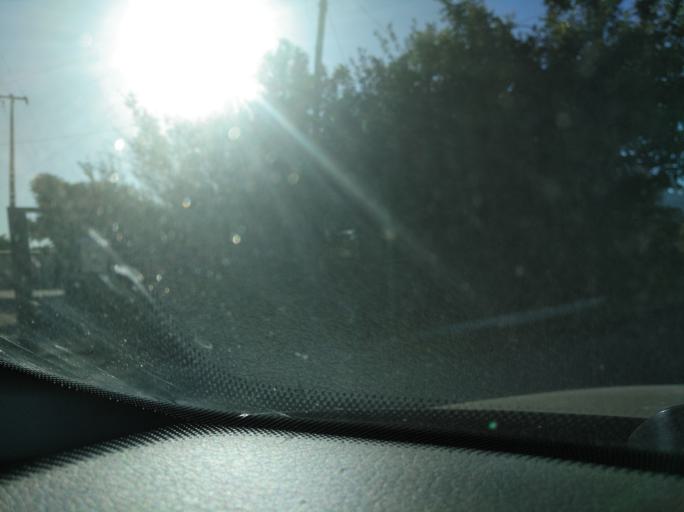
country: PT
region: Faro
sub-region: Vila Real de Santo Antonio
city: Monte Gordo
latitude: 37.1820
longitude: -7.5106
